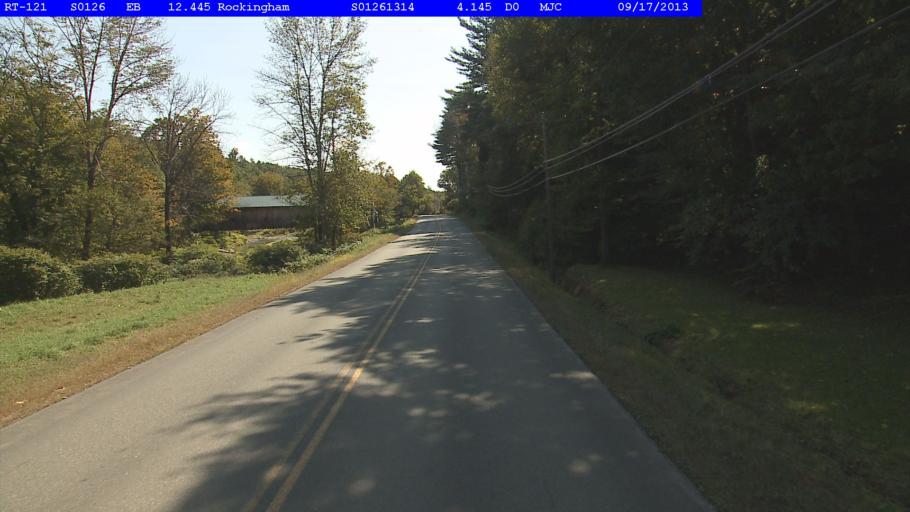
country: US
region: Vermont
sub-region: Windham County
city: Bellows Falls
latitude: 43.1379
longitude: -72.4889
